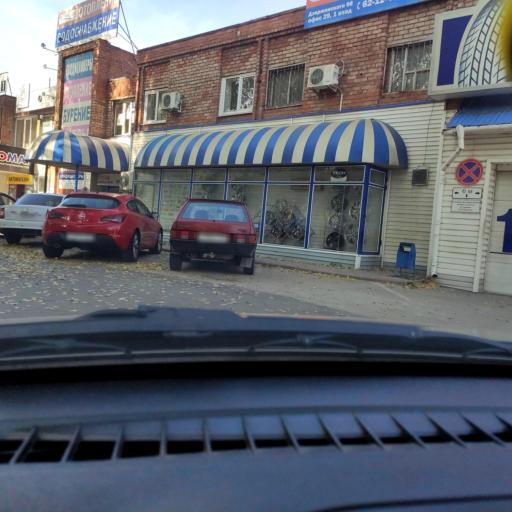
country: RU
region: Samara
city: Tol'yatti
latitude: 53.5392
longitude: 49.2656
